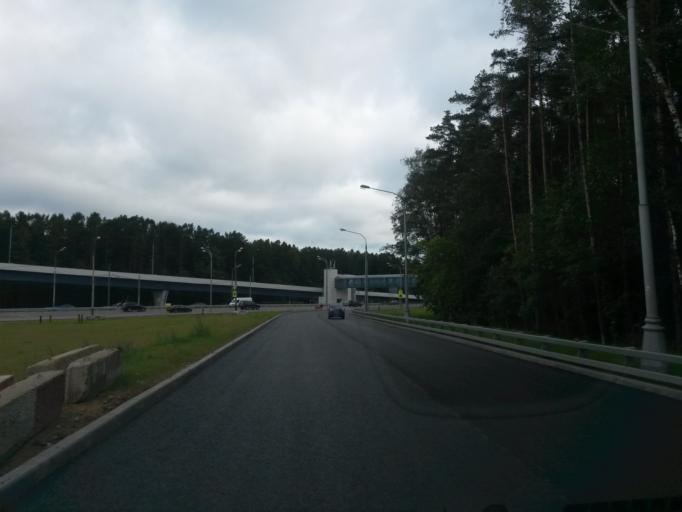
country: RU
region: Moskovskaya
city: Mosrentgen
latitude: 55.6392
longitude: 37.4629
